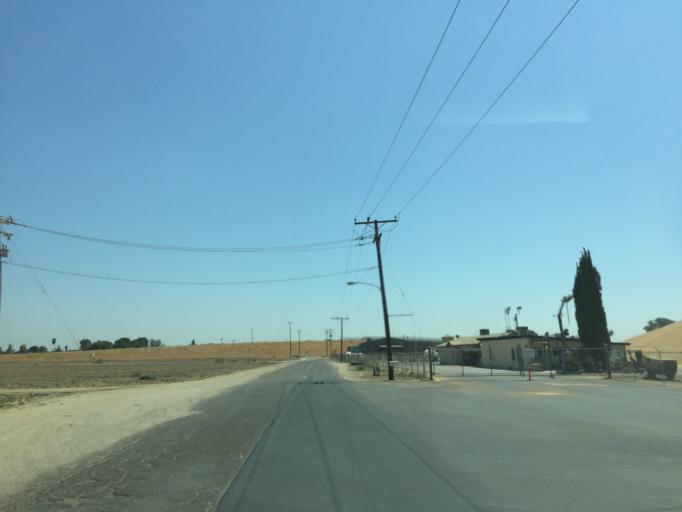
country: US
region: California
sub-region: Tulare County
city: Goshen
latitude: 36.3567
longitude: -119.4214
